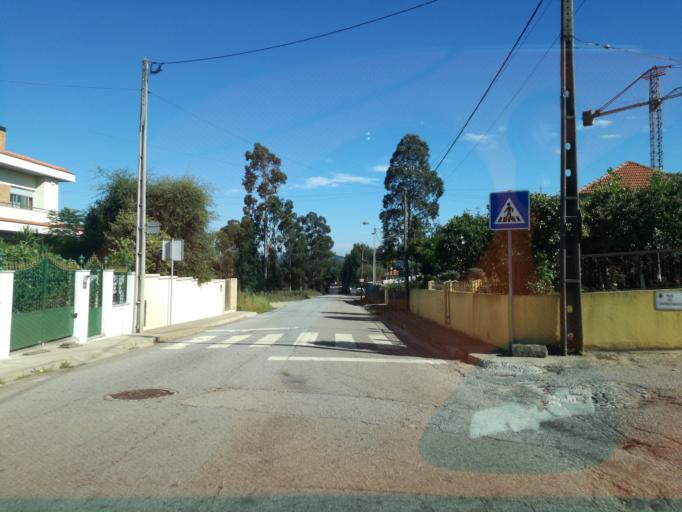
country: PT
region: Porto
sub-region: Trofa
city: Sao Romao do Coronado
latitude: 41.2733
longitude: -8.5392
